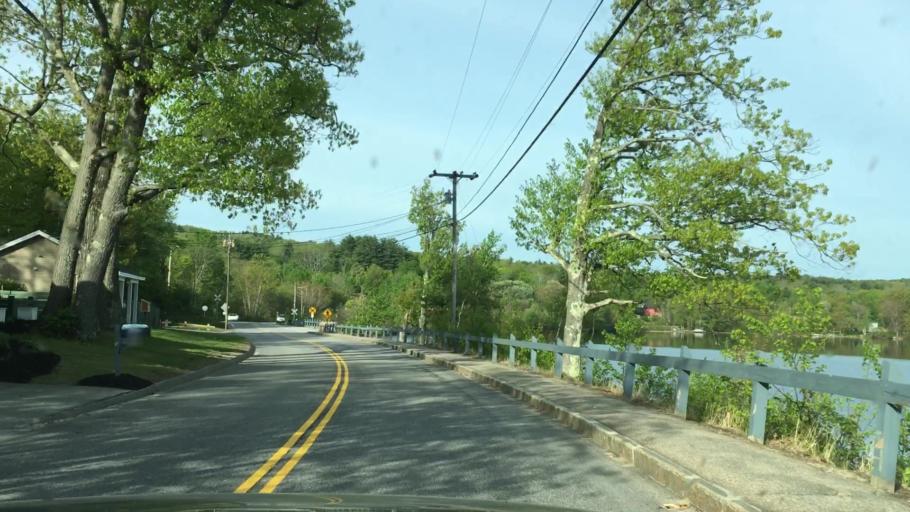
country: US
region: New Hampshire
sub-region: Belknap County
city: Meredith
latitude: 43.6477
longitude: -71.5070
